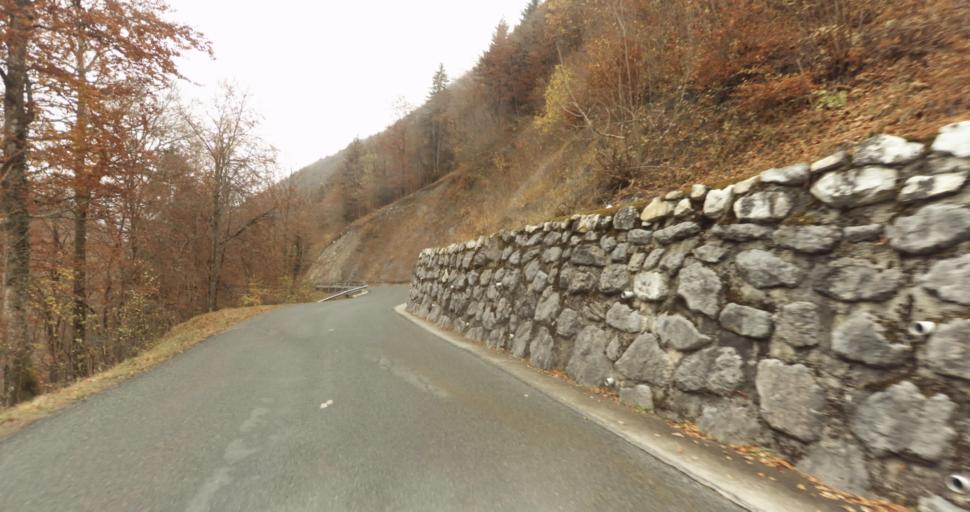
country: FR
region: Rhone-Alpes
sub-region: Departement de la Haute-Savoie
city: Doussard
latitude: 45.7859
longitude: 6.2593
